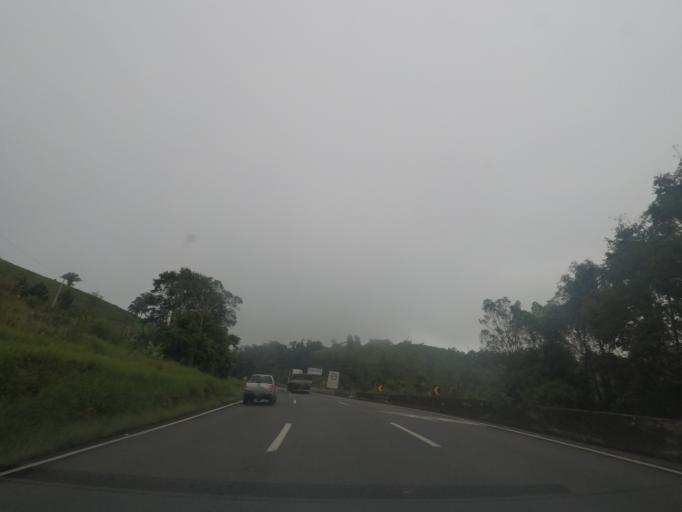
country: BR
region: Parana
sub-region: Antonina
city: Antonina
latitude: -25.0427
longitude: -48.5531
